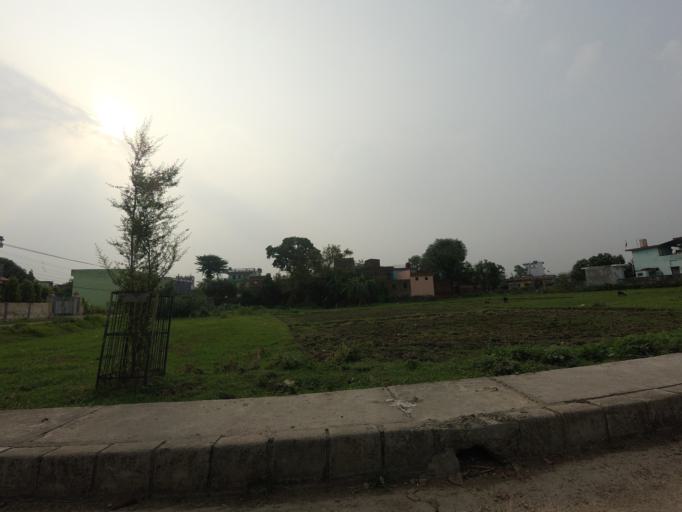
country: NP
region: Western Region
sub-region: Lumbini Zone
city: Bhairahawa
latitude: 27.4930
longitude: 83.4470
